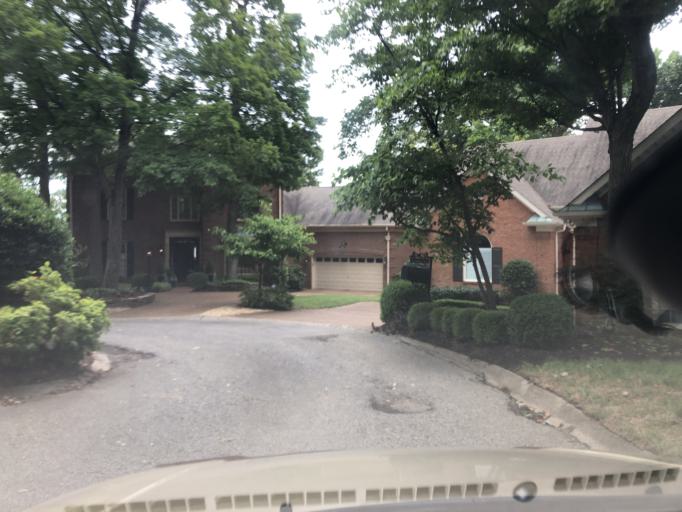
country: US
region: Tennessee
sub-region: Wilson County
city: Green Hill
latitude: 36.2576
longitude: -86.5831
